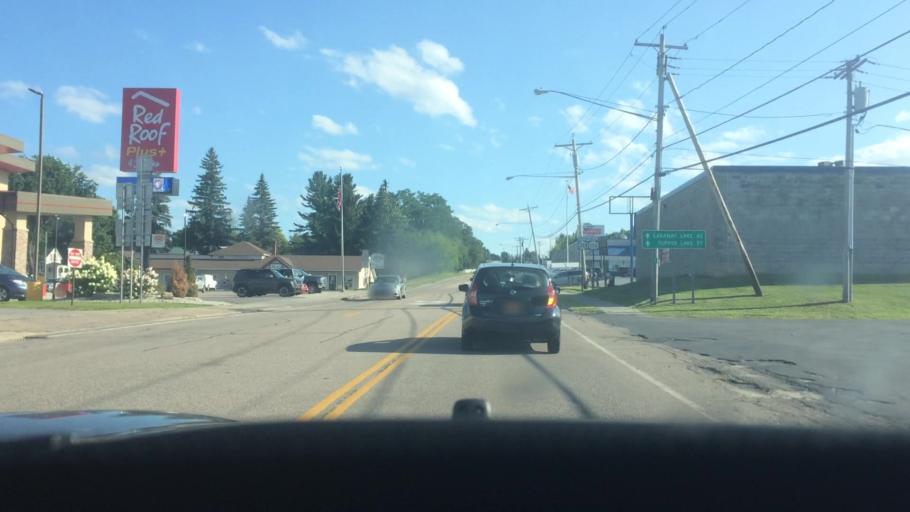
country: US
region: New York
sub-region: Franklin County
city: Malone
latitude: 44.8478
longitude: -74.3009
